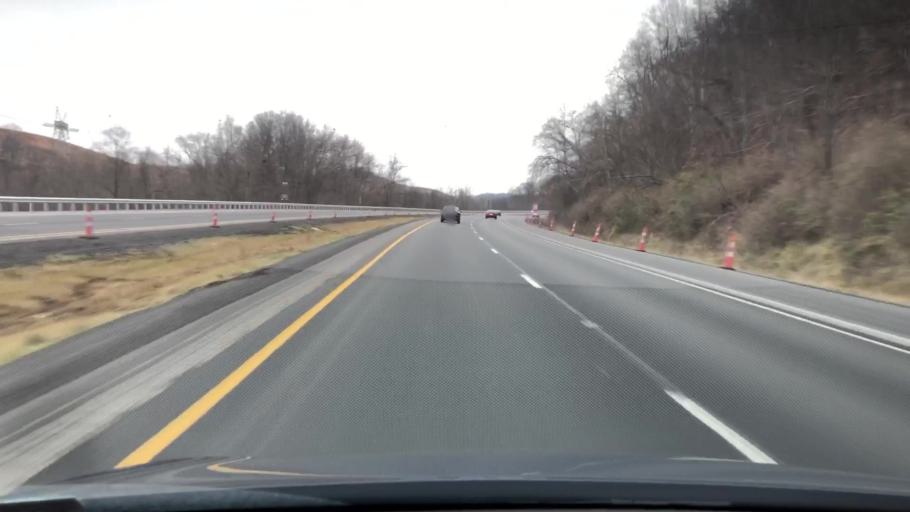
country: US
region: West Virginia
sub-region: Monongalia County
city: Star City
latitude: 39.6749
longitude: -80.0331
